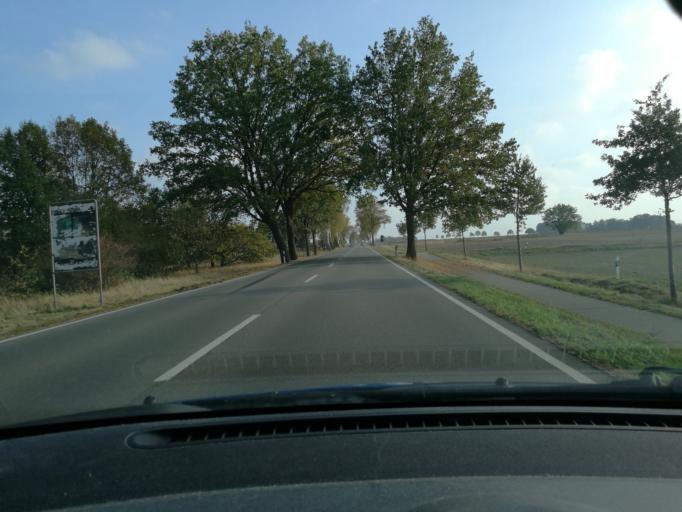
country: DE
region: Lower Saxony
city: Luechow
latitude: 52.9919
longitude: 11.1172
